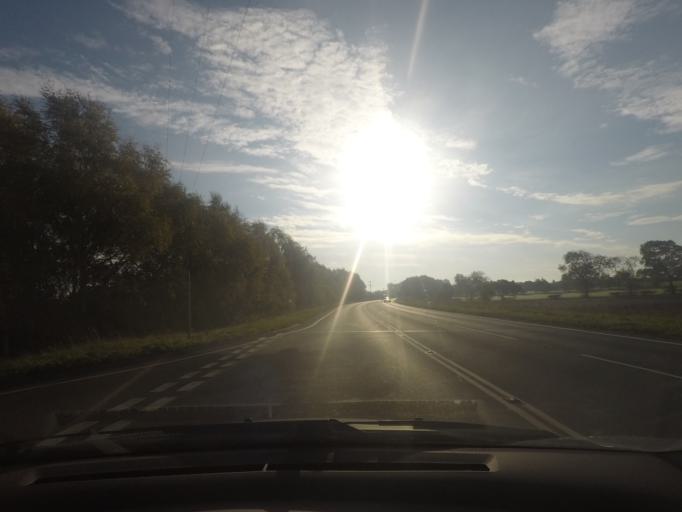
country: GB
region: England
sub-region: East Riding of Yorkshire
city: Londesborough
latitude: 53.8707
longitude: -0.6877
